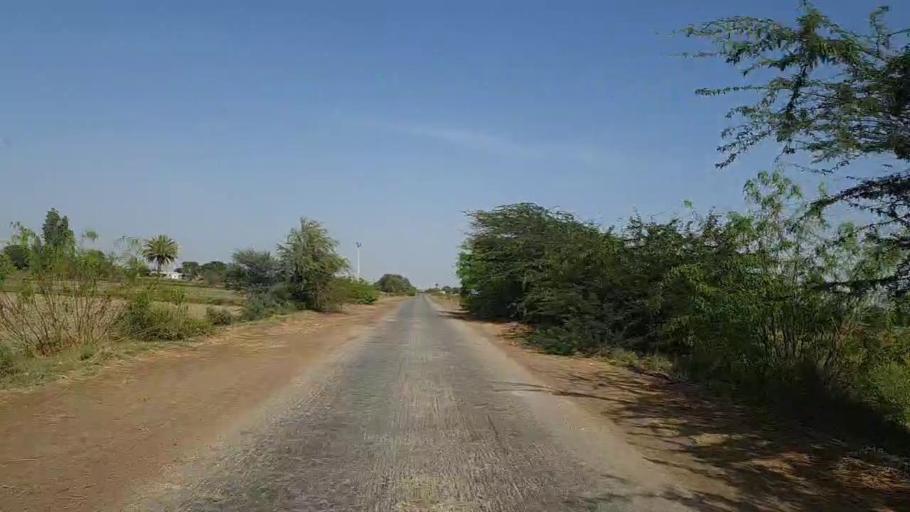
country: PK
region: Sindh
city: Kotri
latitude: 25.1666
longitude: 68.2782
